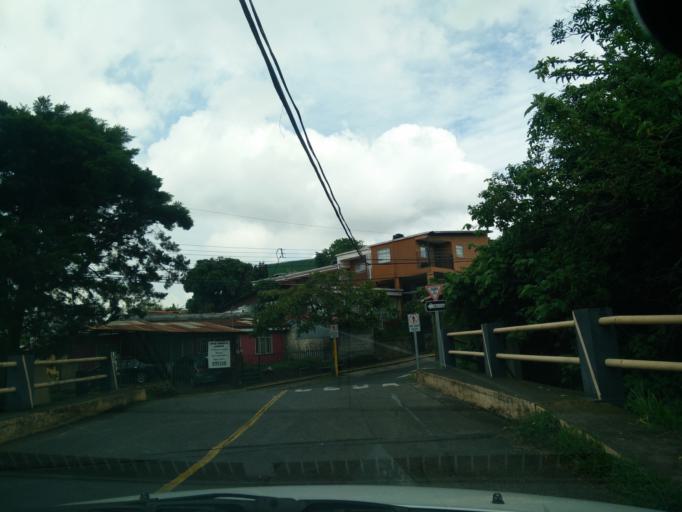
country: CR
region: Heredia
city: San Rafael
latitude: 10.0071
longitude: -84.1039
